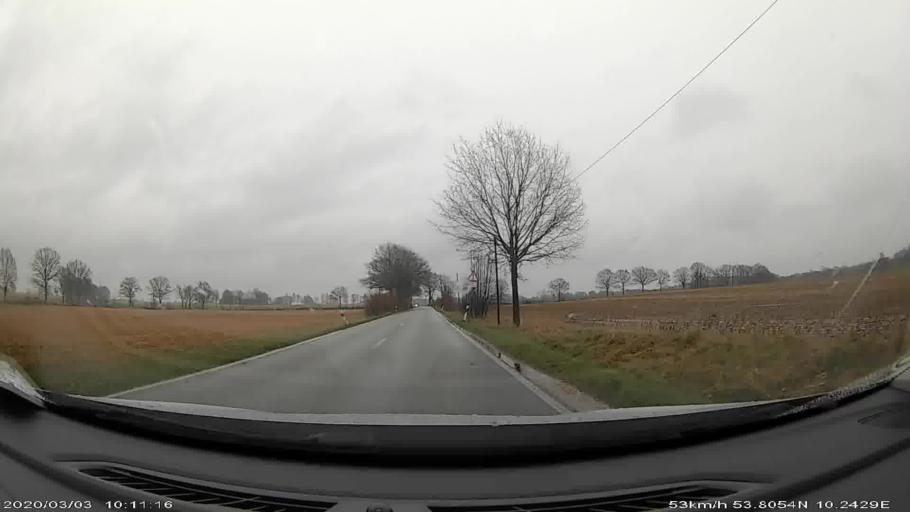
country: DE
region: Schleswig-Holstein
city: Sulfeld
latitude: 53.8055
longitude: 10.2500
